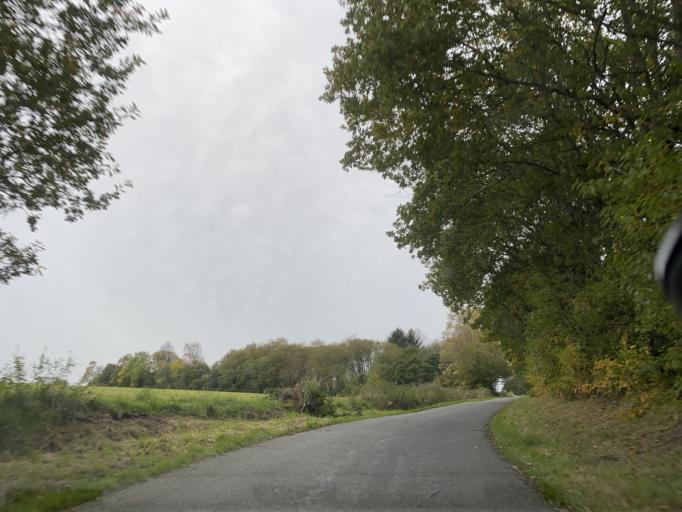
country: DK
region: Central Jutland
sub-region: Skanderborg Kommune
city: Ry
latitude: 56.1957
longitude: 9.7763
